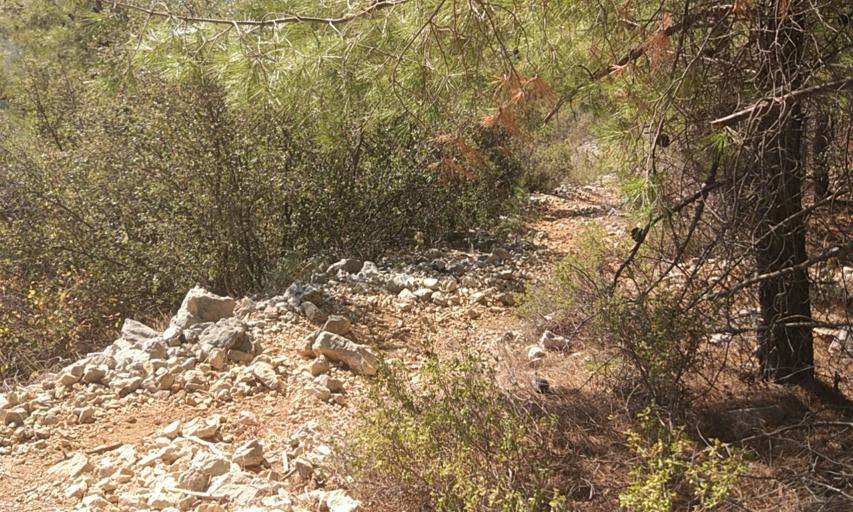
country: TR
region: Antalya
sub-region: Kemer
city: Goeynuek
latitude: 36.6333
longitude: 30.4473
